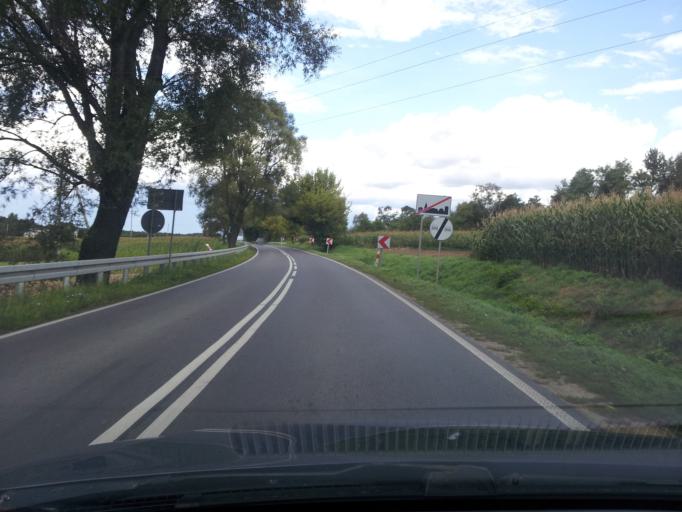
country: PL
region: Kujawsko-Pomorskie
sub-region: Powiat rypinski
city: Rypin
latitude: 53.1247
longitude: 19.3865
